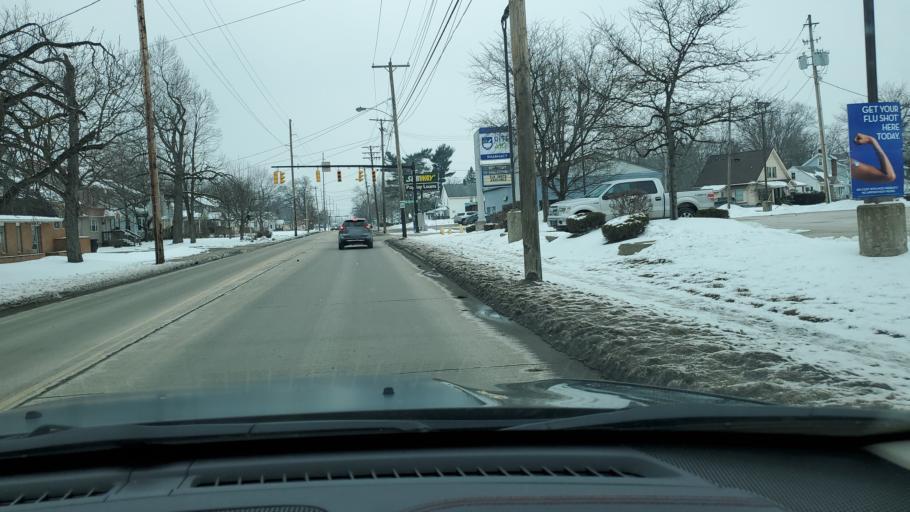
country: US
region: Ohio
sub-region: Trumbull County
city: Warren
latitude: 41.2444
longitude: -80.8425
